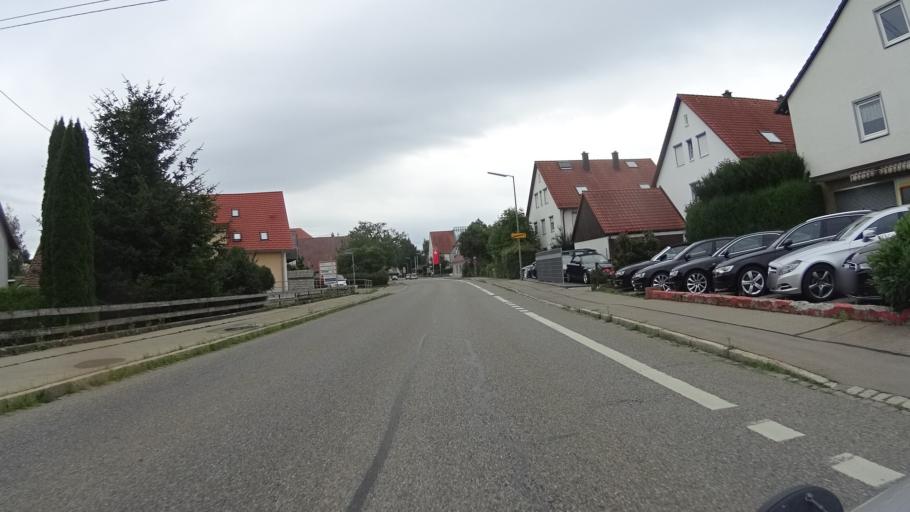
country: DE
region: Bavaria
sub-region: Swabia
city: Heimertingen
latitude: 48.0165
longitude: 10.1604
